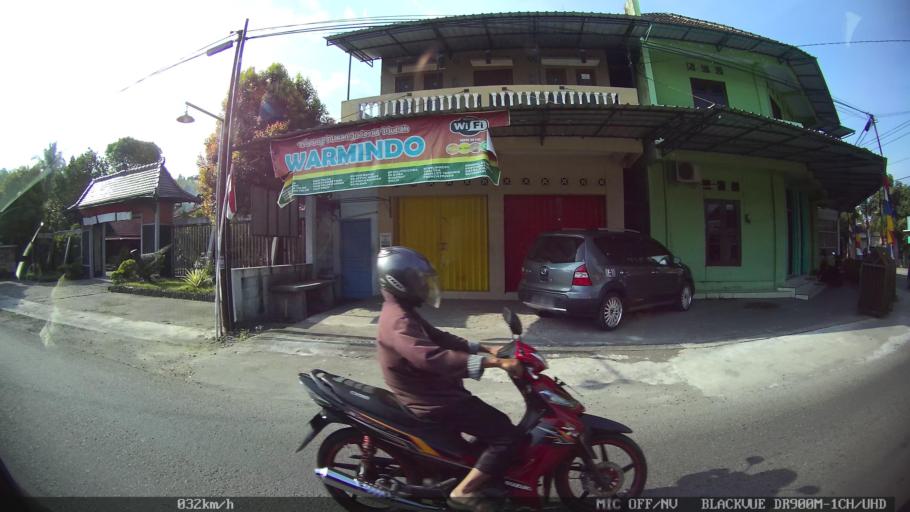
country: ID
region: Daerah Istimewa Yogyakarta
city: Bantul
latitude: -7.8812
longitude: 110.3111
